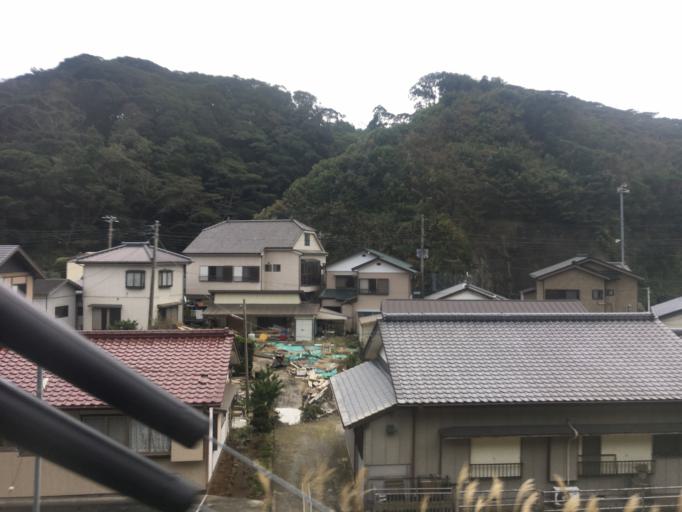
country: JP
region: Chiba
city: Katsuura
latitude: 35.1400
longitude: 140.2771
